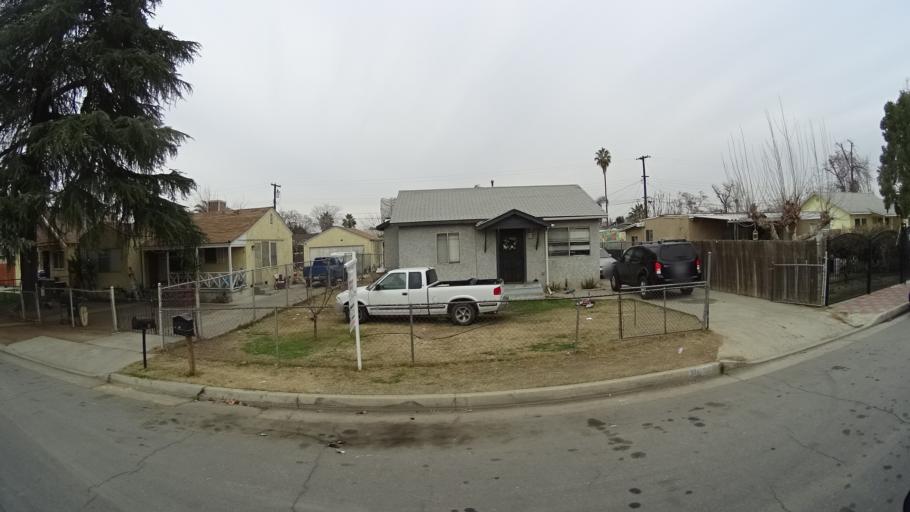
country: US
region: California
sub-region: Kern County
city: Bakersfield
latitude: 35.3566
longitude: -119.0008
